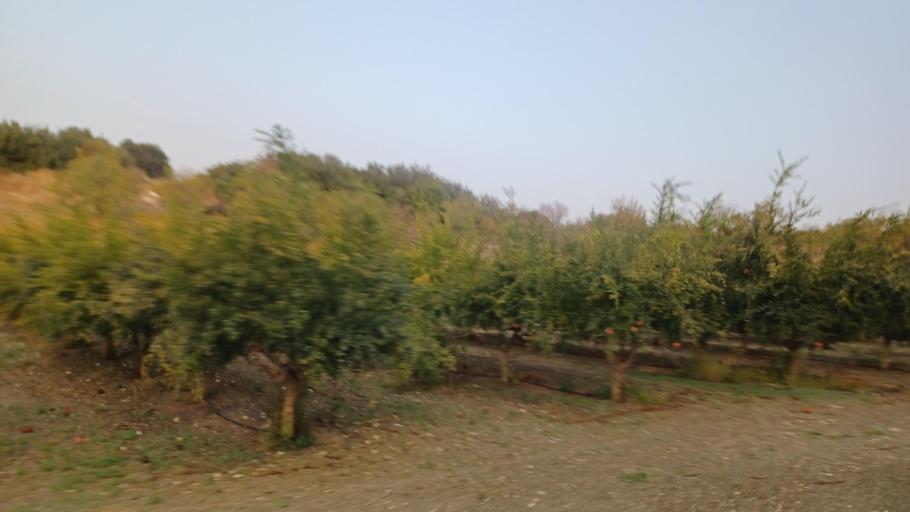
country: CY
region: Pafos
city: Polis
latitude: 34.9591
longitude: 32.5021
